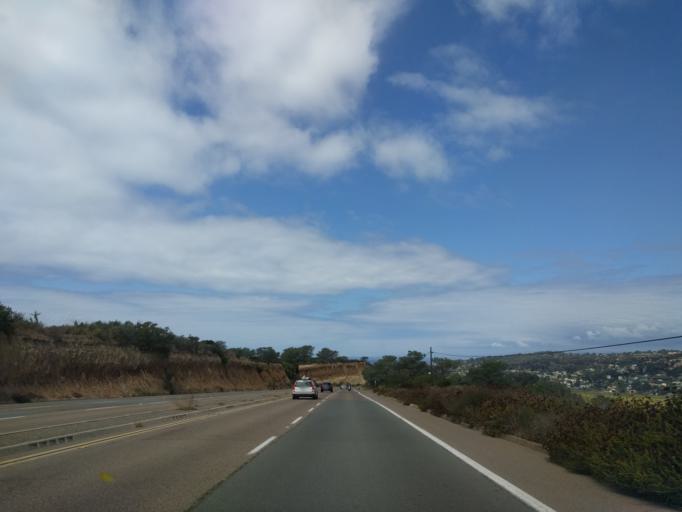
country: US
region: California
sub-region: San Diego County
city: Del Mar
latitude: 32.9156
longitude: -117.2468
